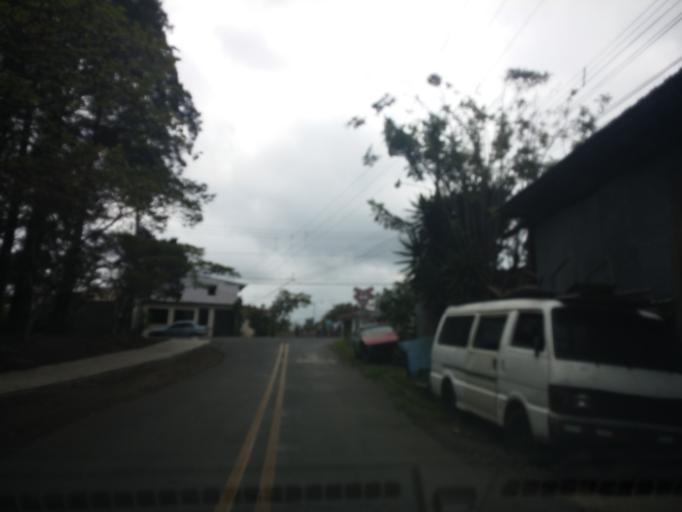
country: CR
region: Heredia
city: Llorente
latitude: 10.0022
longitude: -84.1481
